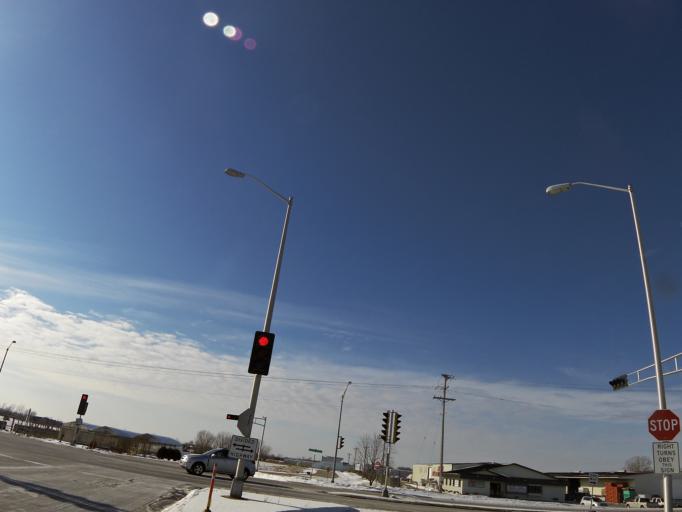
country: US
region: Wisconsin
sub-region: Saint Croix County
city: North Hudson
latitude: 44.9881
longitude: -92.6798
